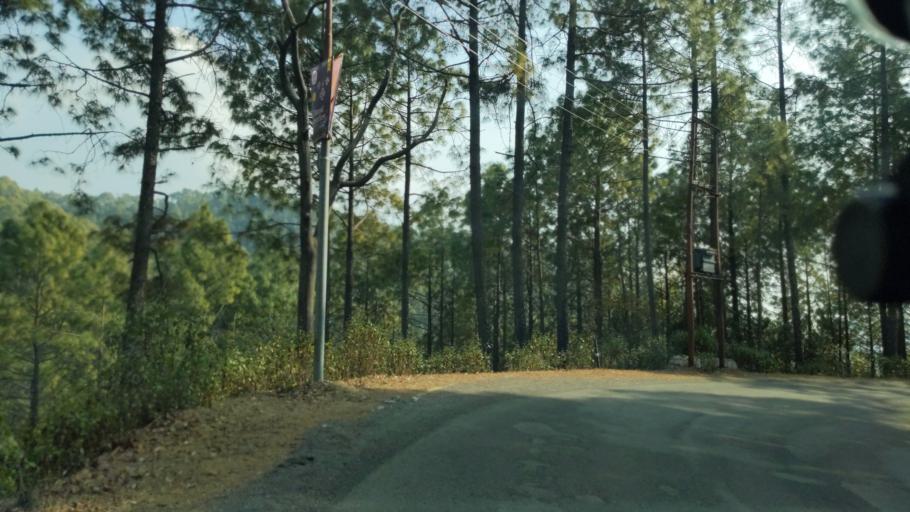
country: IN
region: Uttarakhand
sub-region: Naini Tal
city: Bhowali
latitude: 29.4043
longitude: 79.5395
